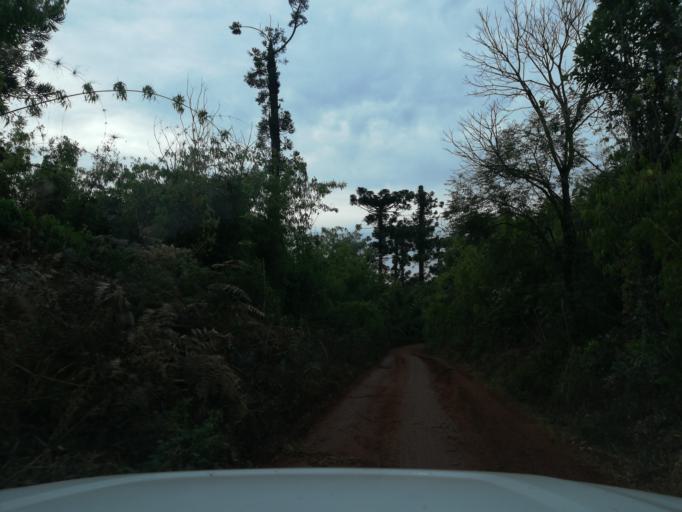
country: AR
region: Misiones
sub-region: Departamento de San Pedro
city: San Pedro
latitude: -26.6312
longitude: -54.0982
